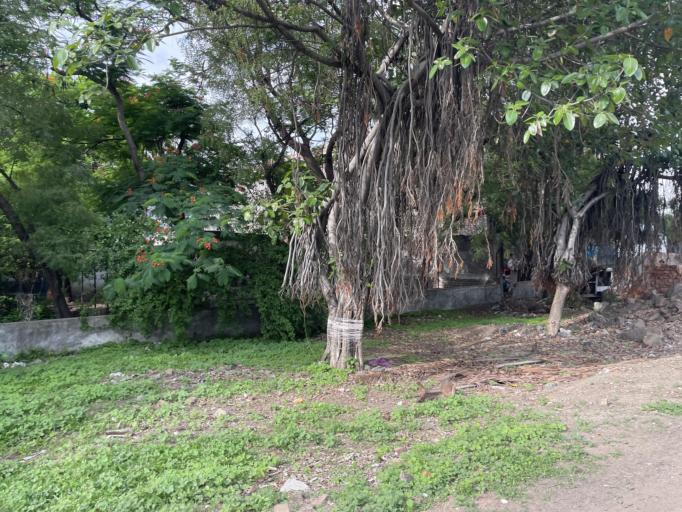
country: IN
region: Maharashtra
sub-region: Aurangabad Division
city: Aurangabad
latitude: 19.8786
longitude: 75.3862
